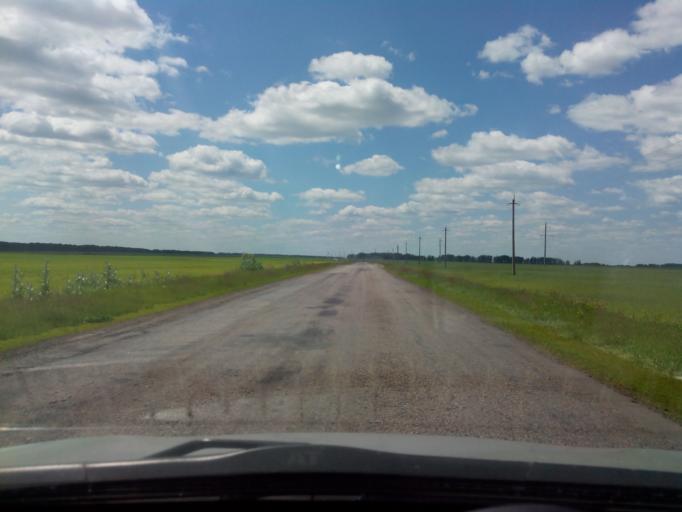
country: RU
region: Voronezj
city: Gribanovskiy
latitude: 51.6187
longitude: 41.8730
